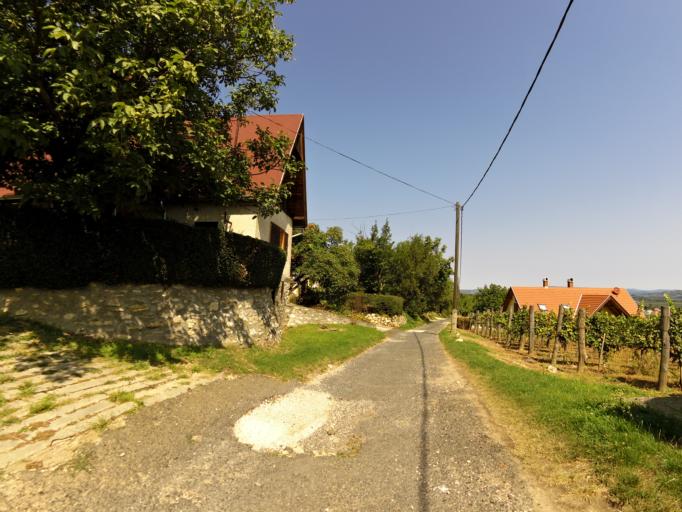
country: HU
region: Zala
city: Vonyarcvashegy
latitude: 46.7955
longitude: 17.3719
